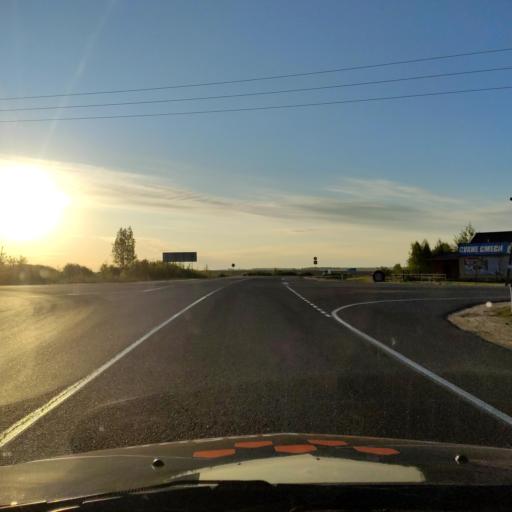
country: RU
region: Orjol
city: Livny
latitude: 52.4495
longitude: 37.6267
